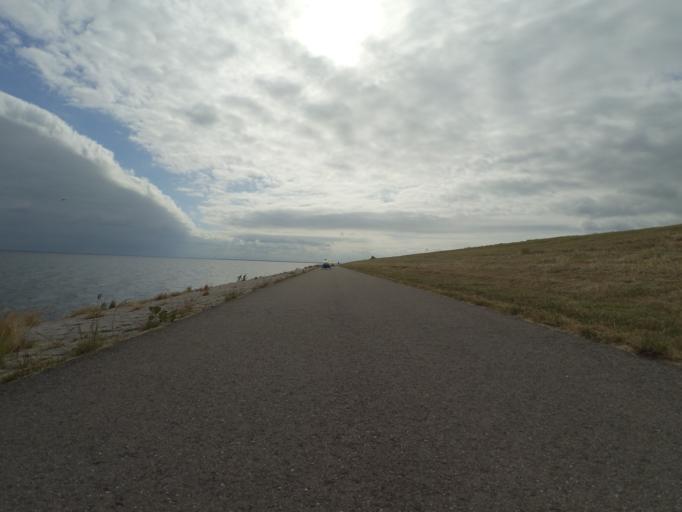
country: NL
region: Zeeland
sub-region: Gemeente Reimerswaal
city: Yerseke
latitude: 51.4451
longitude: 4.0999
